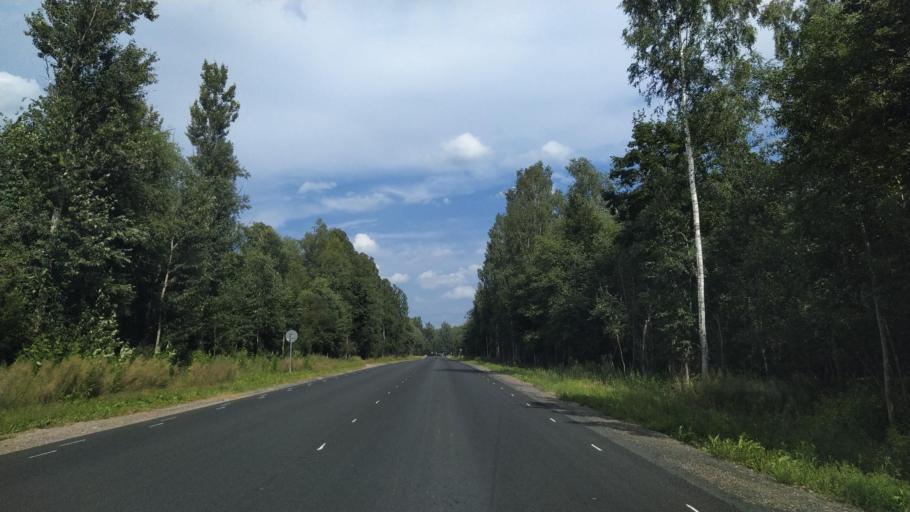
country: RU
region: Pskov
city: Vybor
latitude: 57.7112
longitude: 28.9149
